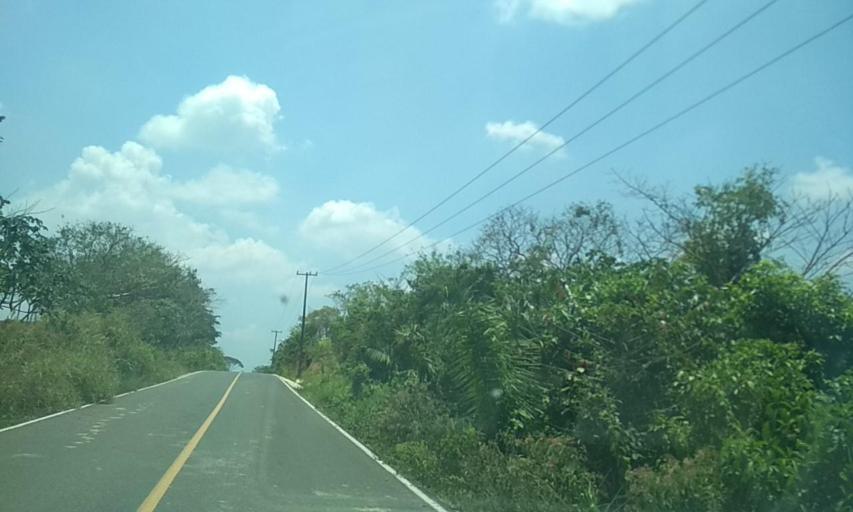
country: MX
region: Tabasco
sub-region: Huimanguillo
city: Francisco Rueda
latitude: 17.7622
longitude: -94.0585
